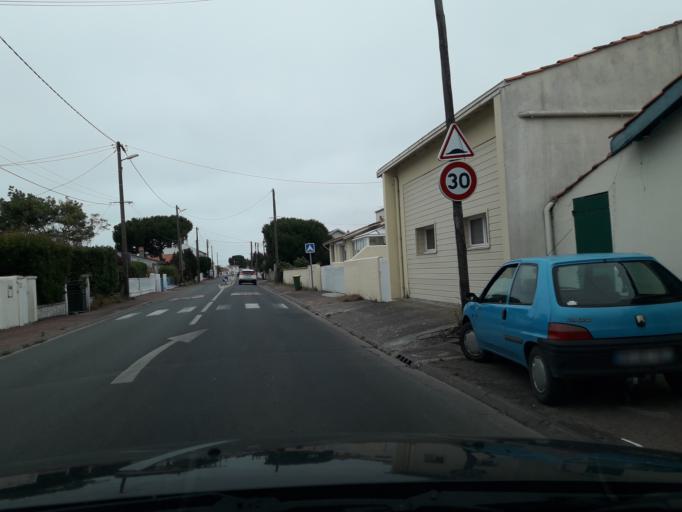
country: FR
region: Poitou-Charentes
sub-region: Departement de la Charente-Maritime
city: Boyard-Ville
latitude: 45.9661
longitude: -1.2468
